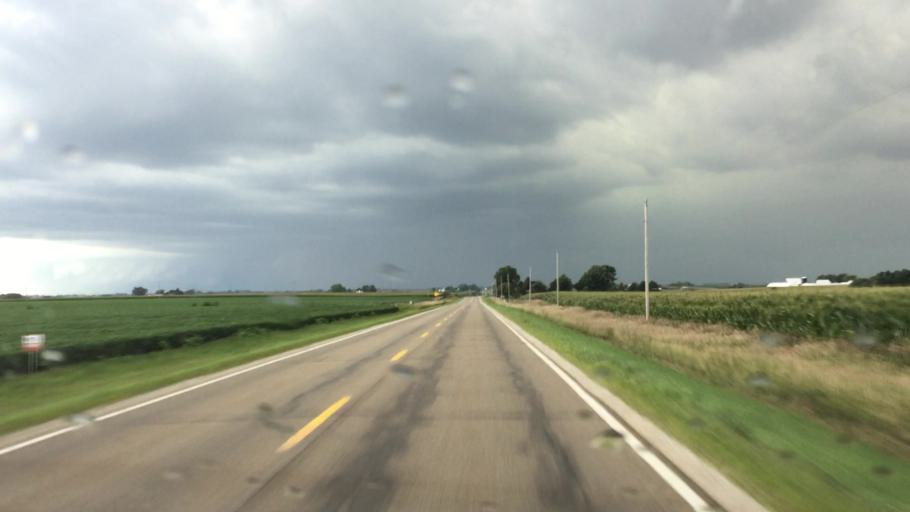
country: US
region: Iowa
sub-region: Henry County
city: Mount Pleasant
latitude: 40.7844
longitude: -91.5193
